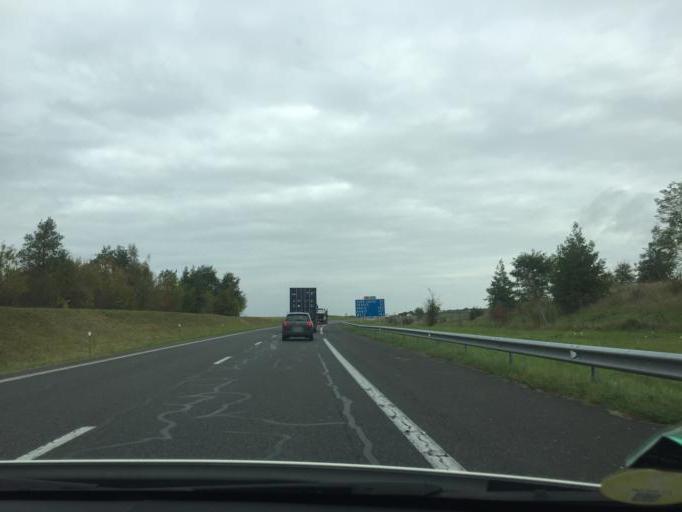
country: FR
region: Centre
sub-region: Departement du Loiret
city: Courtenay
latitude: 48.0571
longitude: 3.1077
